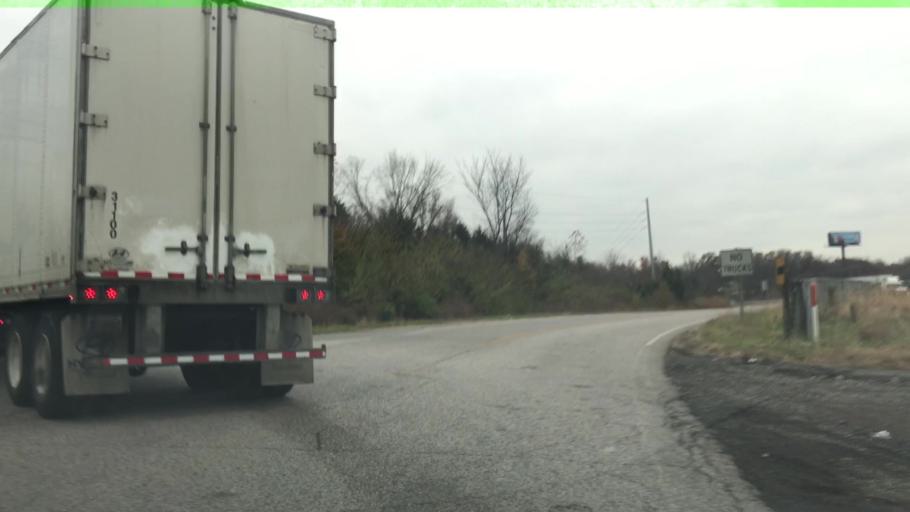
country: US
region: Missouri
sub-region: Clay County
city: Claycomo
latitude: 39.2024
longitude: -94.4908
